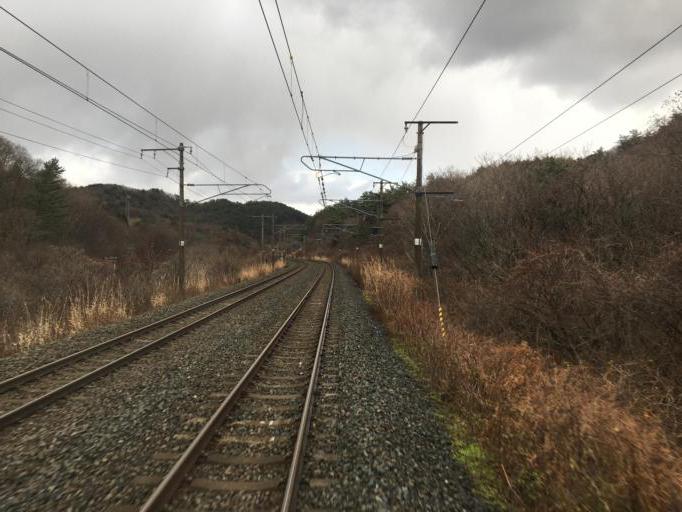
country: JP
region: Aomori
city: Aomori Shi
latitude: 40.9133
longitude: 140.8735
